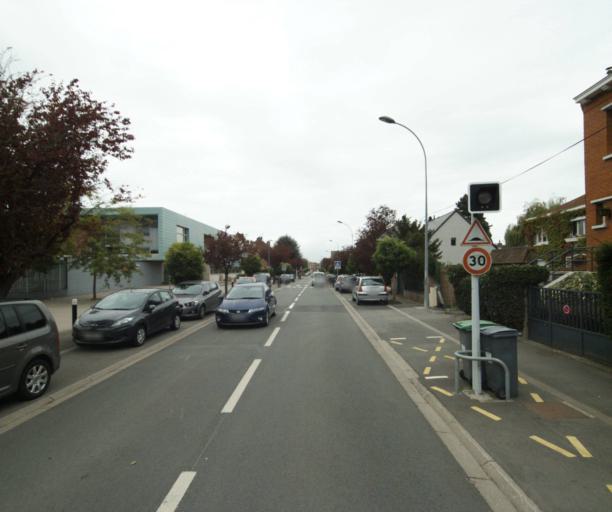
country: FR
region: Nord-Pas-de-Calais
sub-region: Departement du Nord
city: Lambersart
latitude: 50.6483
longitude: 3.0278
